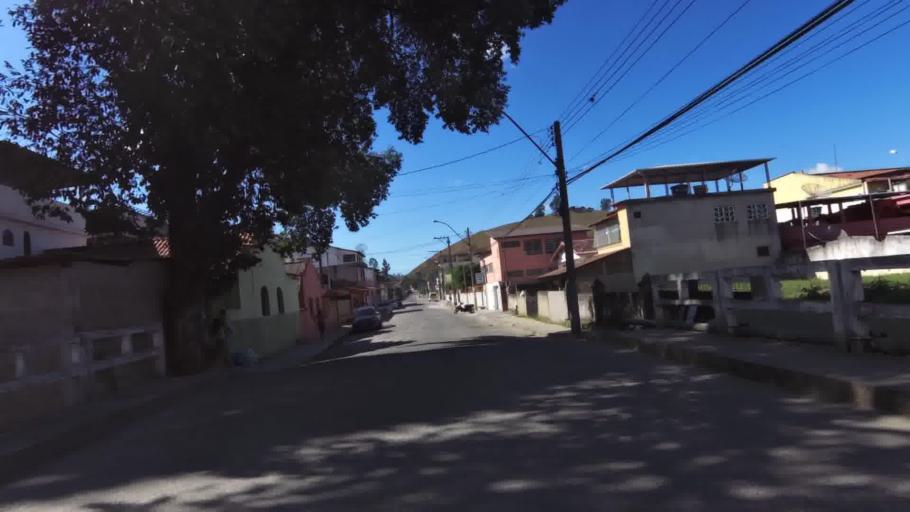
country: BR
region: Espirito Santo
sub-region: Rio Novo Do Sul
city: Rio Novo do Sul
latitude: -20.8627
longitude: -40.9328
